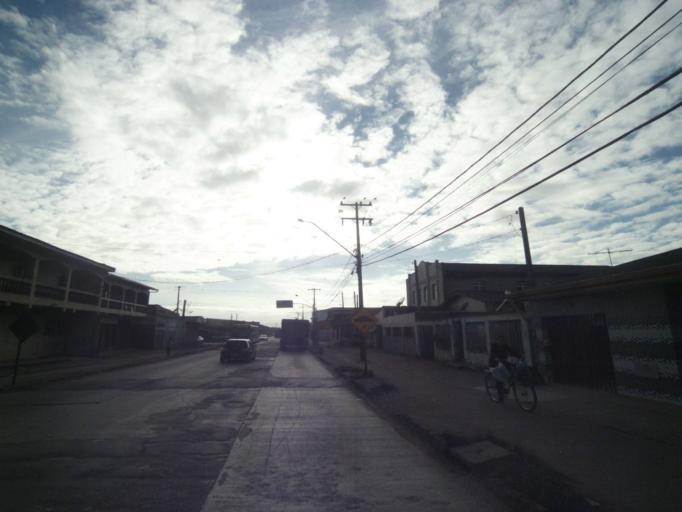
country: BR
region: Parana
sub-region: Paranagua
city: Paranagua
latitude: -25.5197
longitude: -48.5435
